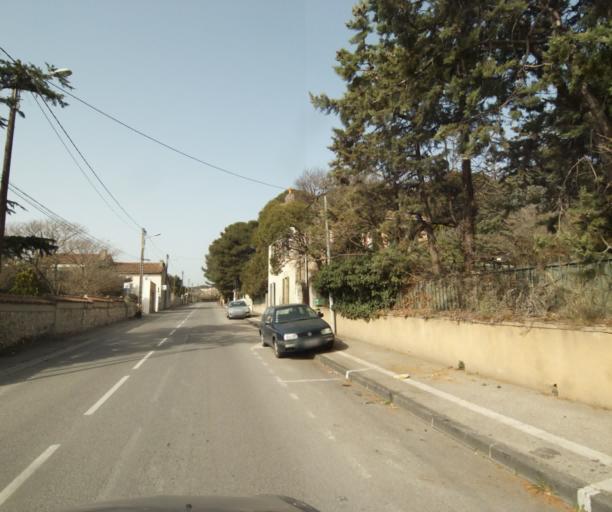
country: FR
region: Provence-Alpes-Cote d'Azur
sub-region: Departement des Bouches-du-Rhone
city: Marseille 15
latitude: 43.3892
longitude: 5.3448
